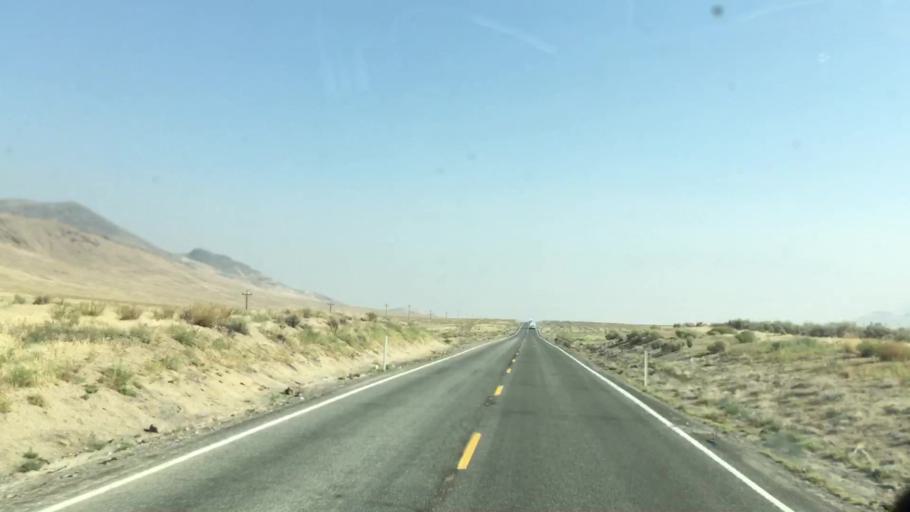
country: US
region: Nevada
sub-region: Lyon County
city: Fernley
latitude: 40.4000
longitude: -119.3337
